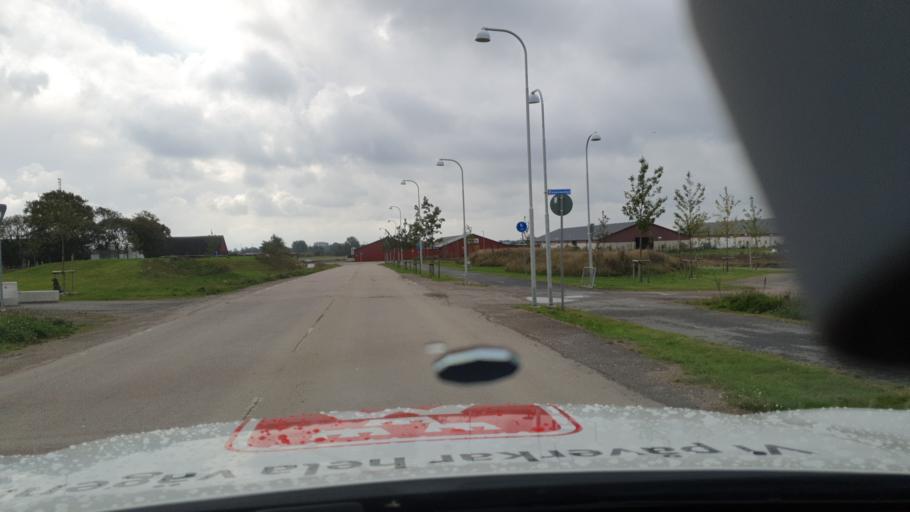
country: SE
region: Skane
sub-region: Vellinge Kommun
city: Vellinge
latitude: 55.4725
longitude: 13.0425
